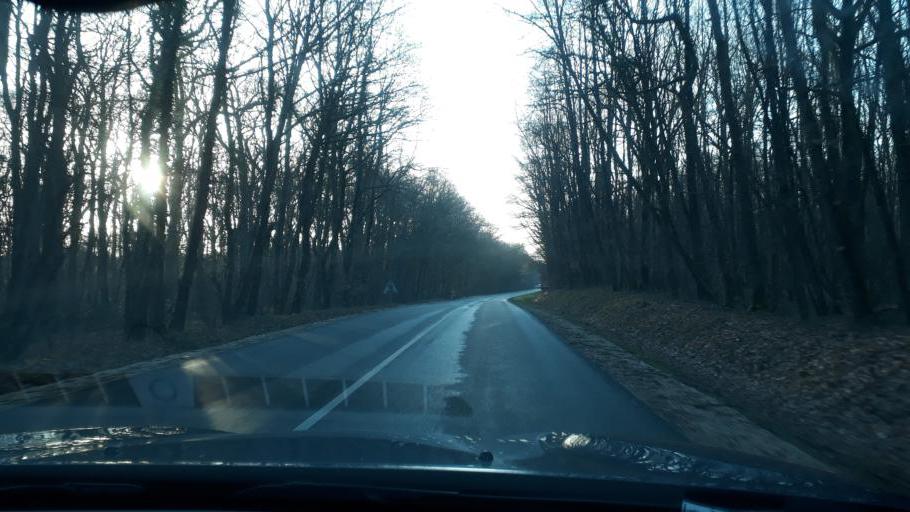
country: FR
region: Centre
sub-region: Departement du Loiret
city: Neuville-aux-Bois
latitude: 48.0434
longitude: 2.0621
